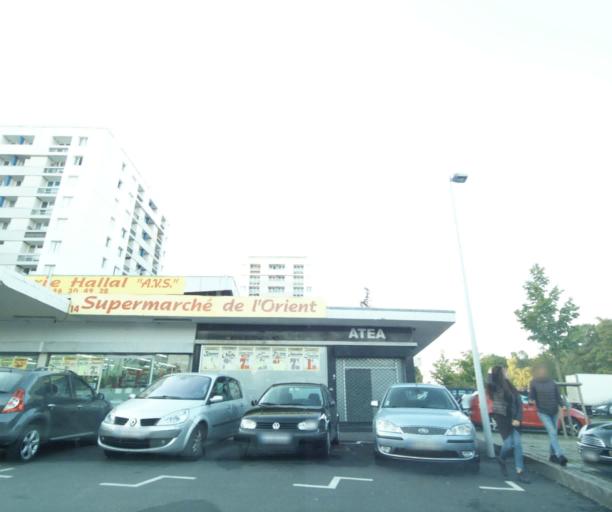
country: FR
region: Ile-de-France
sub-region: Departement des Hauts-de-Seine
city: Meudon
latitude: 48.7862
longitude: 2.2371
